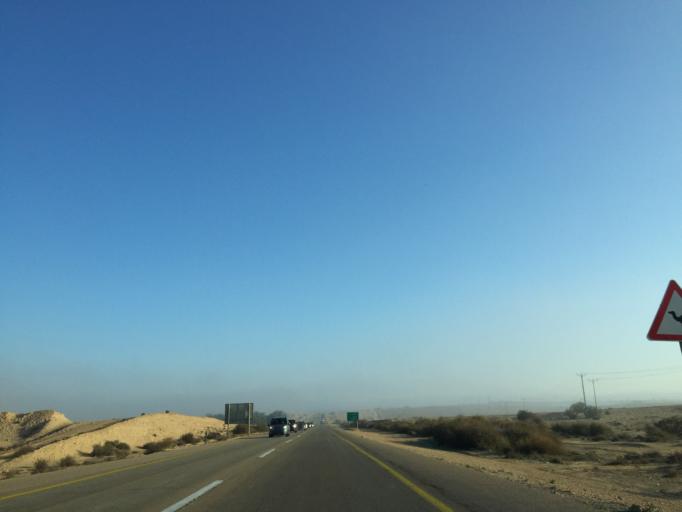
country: IL
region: Southern District
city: Yeroham
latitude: 30.9993
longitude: 34.9438
